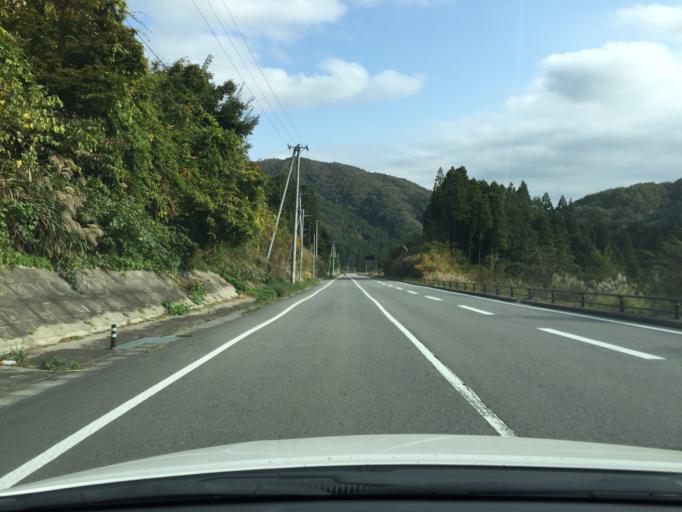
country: JP
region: Ibaraki
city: Kitaibaraki
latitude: 36.9745
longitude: 140.6117
